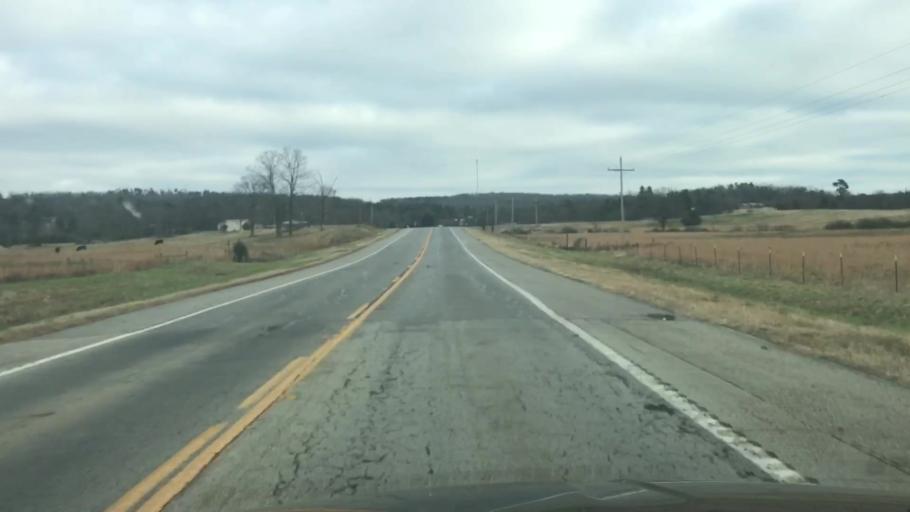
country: US
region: Arkansas
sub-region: Scott County
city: Waldron
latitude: 34.8042
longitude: -94.0407
